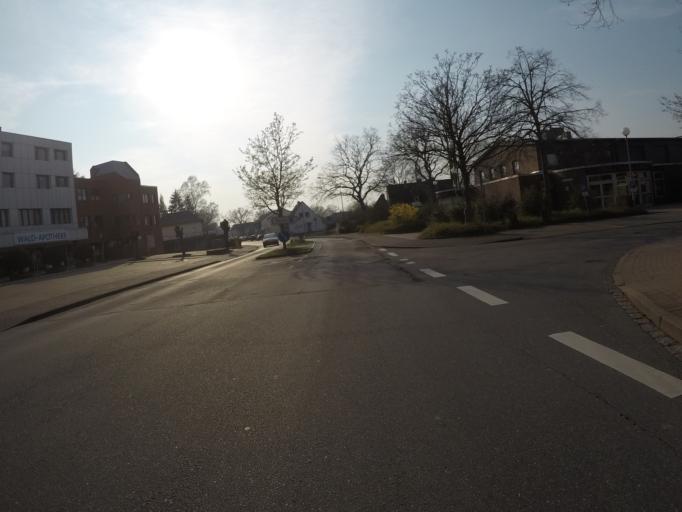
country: DE
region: Schleswig-Holstein
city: Wahlstedt
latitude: 53.9518
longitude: 10.2097
